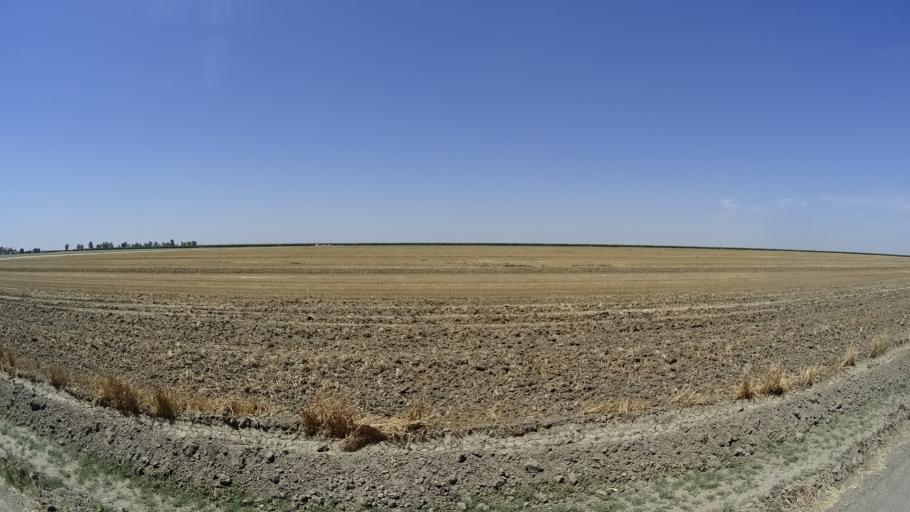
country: US
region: California
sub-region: Kings County
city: Corcoran
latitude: 36.1178
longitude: -119.5812
